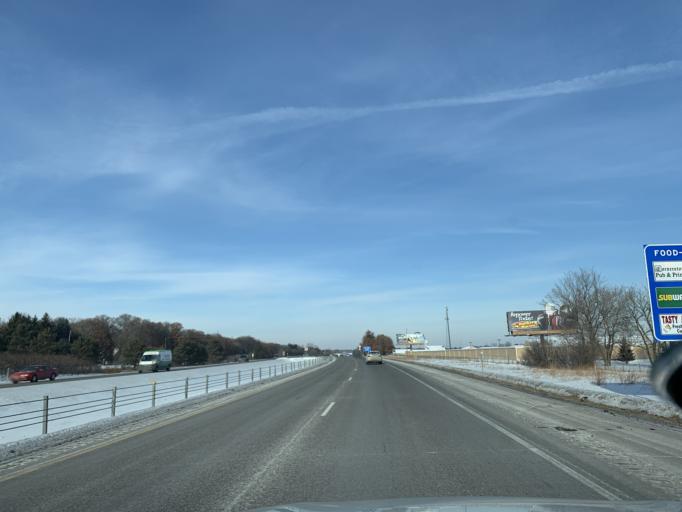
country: US
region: Minnesota
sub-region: Chisago County
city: Wyoming
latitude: 45.3246
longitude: -93.0033
